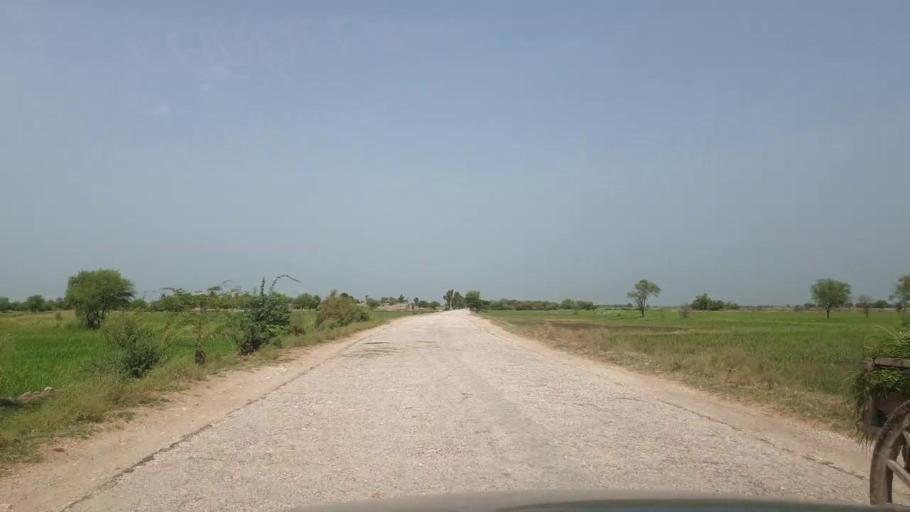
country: PK
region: Sindh
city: Garhi Yasin
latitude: 27.8561
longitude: 68.4195
